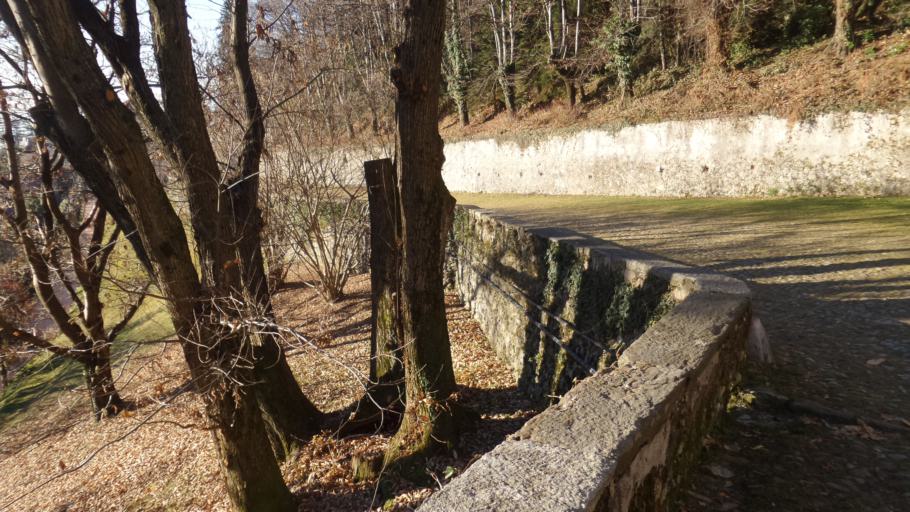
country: IT
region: Lombardy
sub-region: Provincia di Varese
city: Casciago
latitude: 45.8530
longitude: 8.7974
